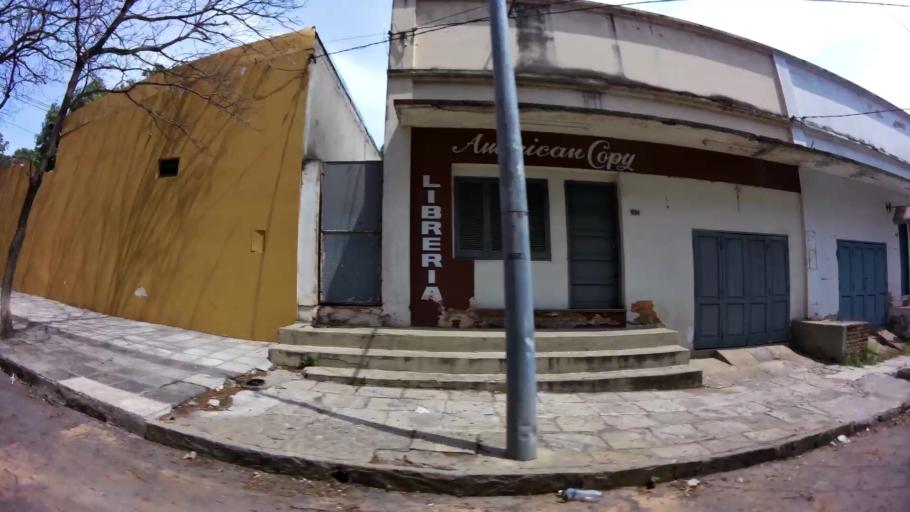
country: PY
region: Asuncion
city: Asuncion
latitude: -25.2792
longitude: -57.5995
